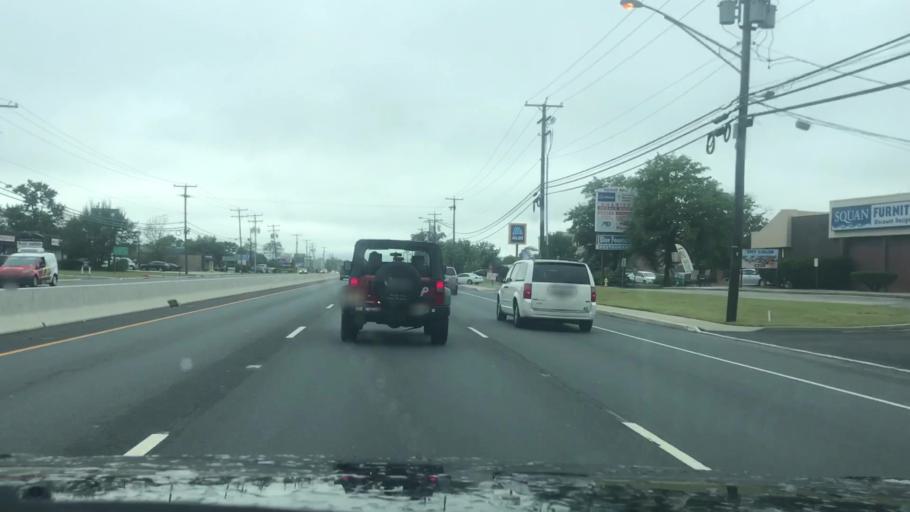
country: US
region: New Jersey
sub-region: Ocean County
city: Holiday City South
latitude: 39.9695
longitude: -74.2327
